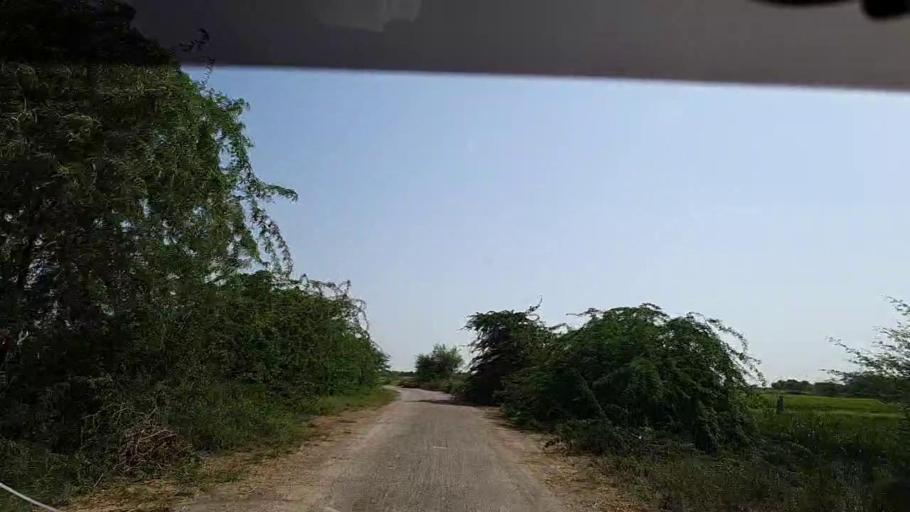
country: PK
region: Sindh
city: Badin
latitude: 24.6279
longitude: 68.7827
